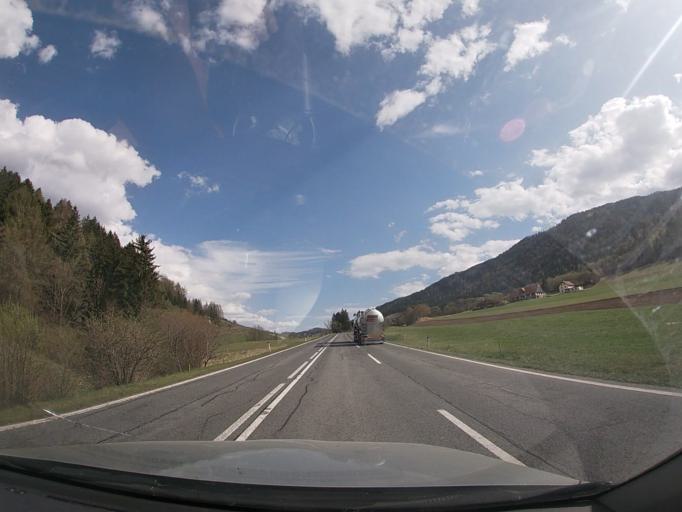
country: AT
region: Styria
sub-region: Politischer Bezirk Murau
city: Sankt Lorenzen bei Scheifling
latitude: 47.1356
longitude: 14.4340
